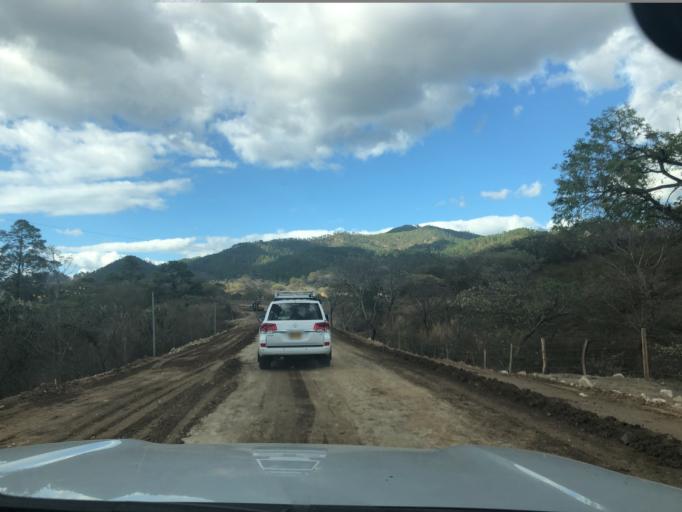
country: NI
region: Nueva Segovia
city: Ocotal
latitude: 13.6597
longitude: -86.6136
